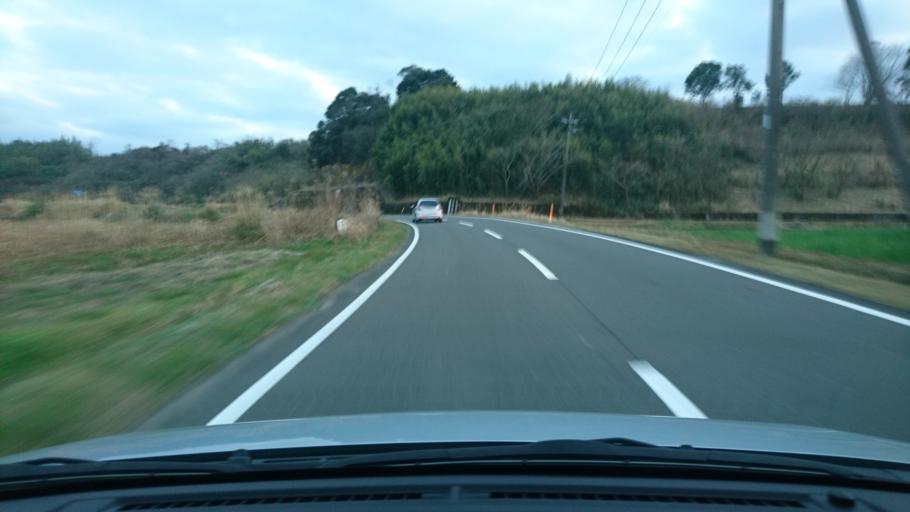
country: JP
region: Miyazaki
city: Miyazaki-shi
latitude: 31.8407
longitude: 131.4072
